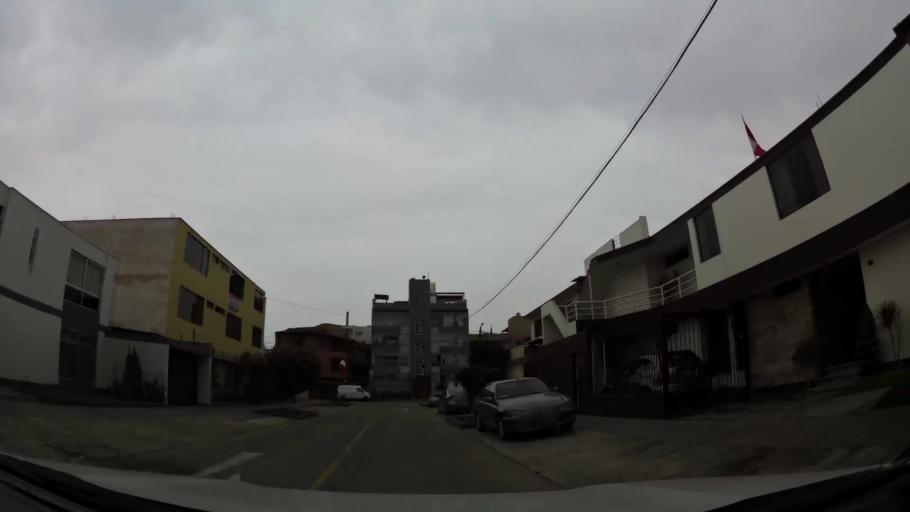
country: PE
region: Lima
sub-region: Lima
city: Surco
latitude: -12.1195
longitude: -76.9902
